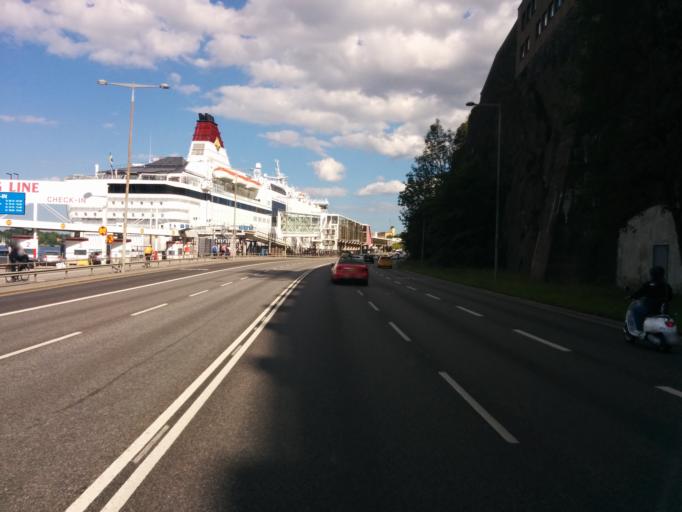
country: SE
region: Stockholm
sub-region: Stockholms Kommun
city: OEstermalm
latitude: 59.3173
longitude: 18.0897
